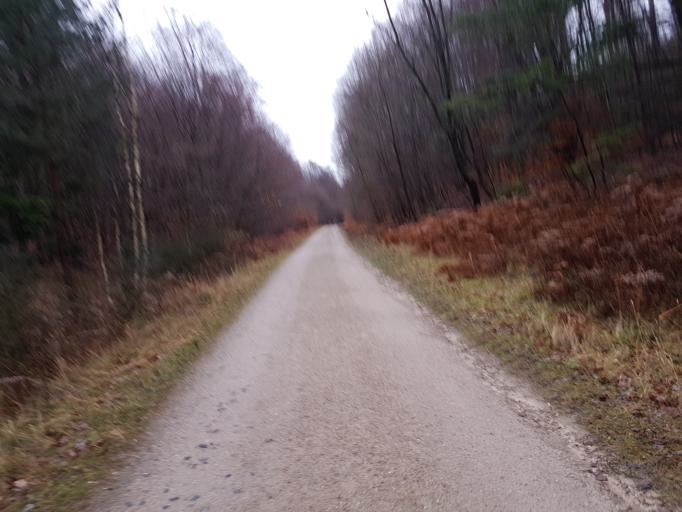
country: DE
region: Mecklenburg-Vorpommern
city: Ostseebad Binz
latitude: 54.3910
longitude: 13.6323
